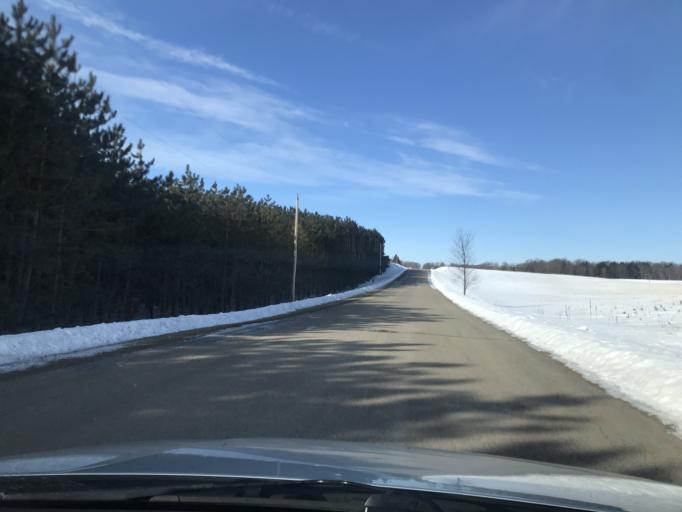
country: US
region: Wisconsin
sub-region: Oconto County
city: Oconto Falls
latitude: 44.9388
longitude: -88.2112
